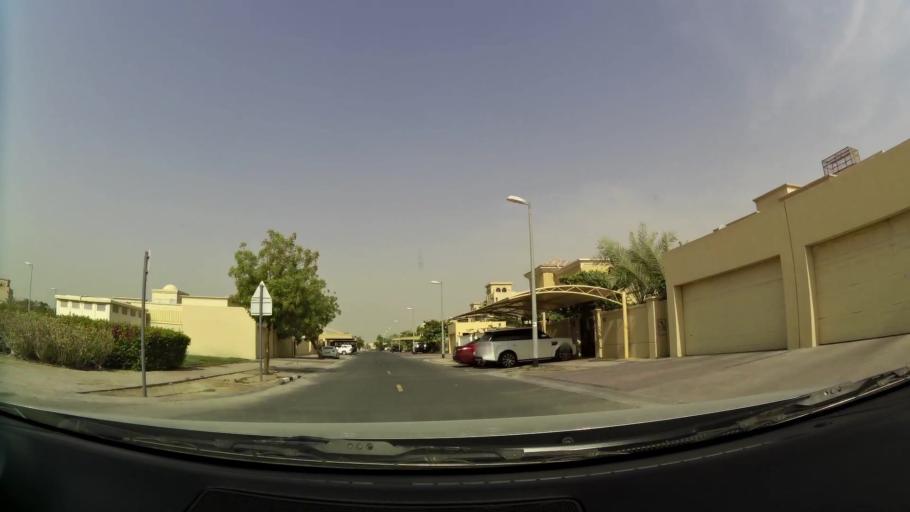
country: AE
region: Ash Shariqah
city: Sharjah
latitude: 25.2626
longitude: 55.4458
